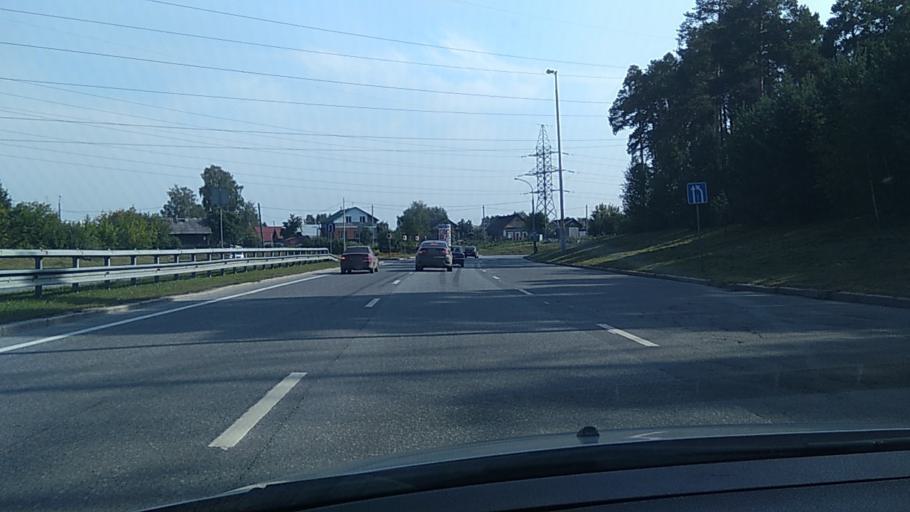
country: RU
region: Sverdlovsk
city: Yekaterinburg
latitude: 56.8860
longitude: 60.5522
